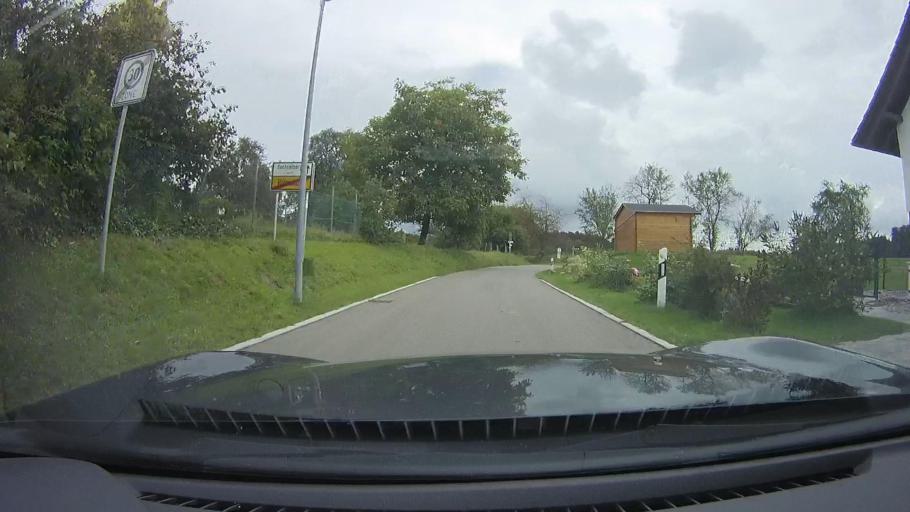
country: DE
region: Baden-Wuerttemberg
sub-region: Regierungsbezirk Stuttgart
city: Murrhardt
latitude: 48.9528
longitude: 9.5538
